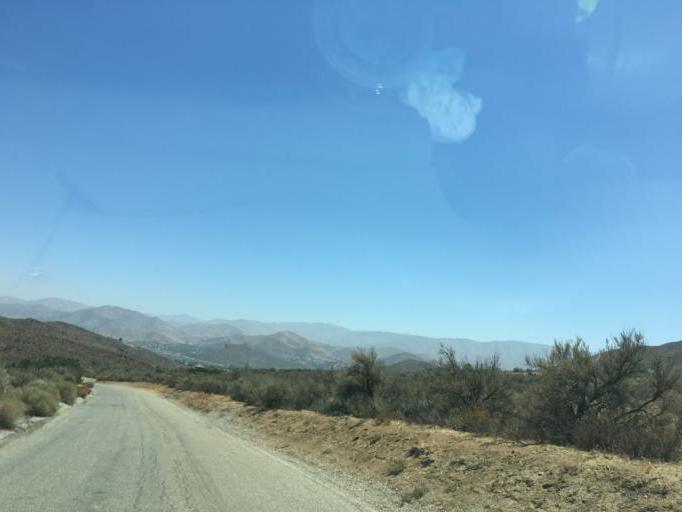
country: US
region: California
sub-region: Los Angeles County
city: Acton
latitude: 34.4780
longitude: -118.2238
